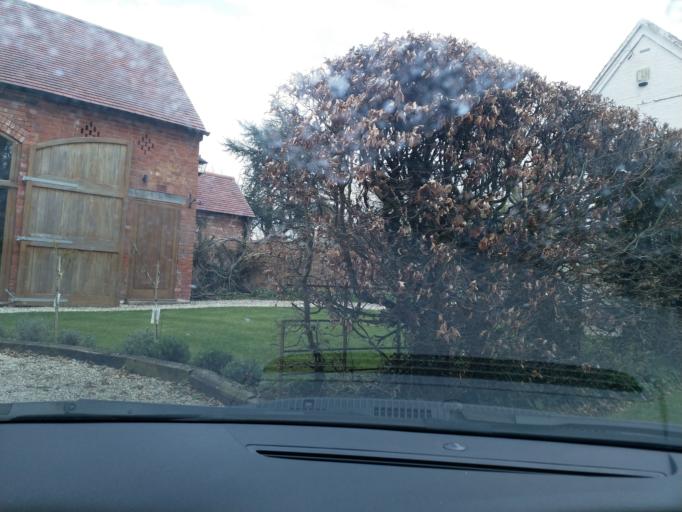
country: GB
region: England
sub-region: Warwickshire
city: Henley in Arden
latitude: 52.2937
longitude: -1.7290
